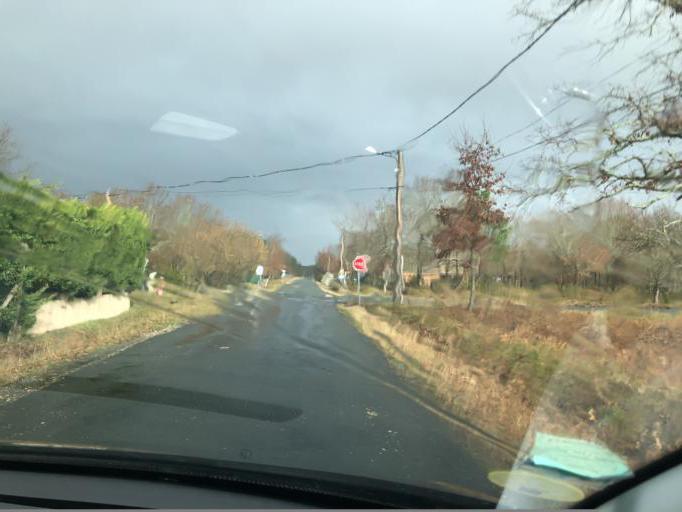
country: FR
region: Aquitaine
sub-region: Departement de la Gironde
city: Hourtin
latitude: 45.1769
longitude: -1.0510
